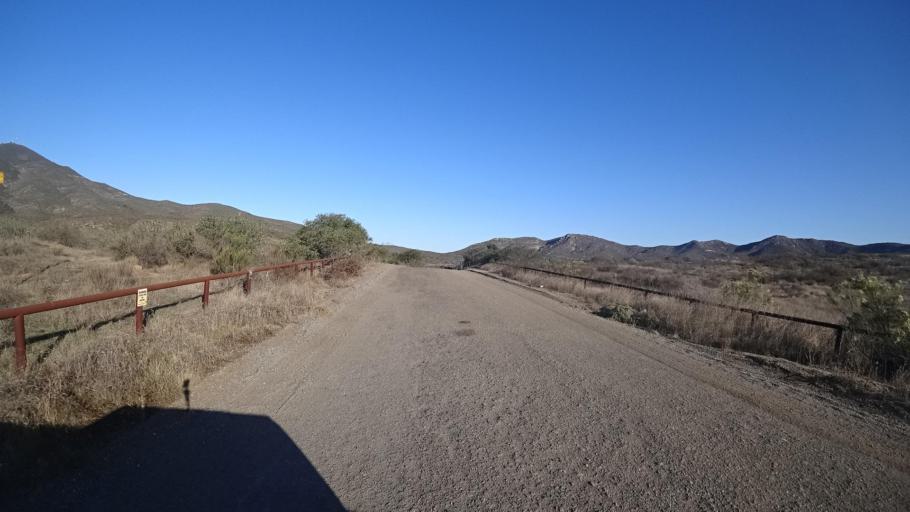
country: US
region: California
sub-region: San Diego County
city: Jamul
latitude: 32.6970
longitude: -116.9048
